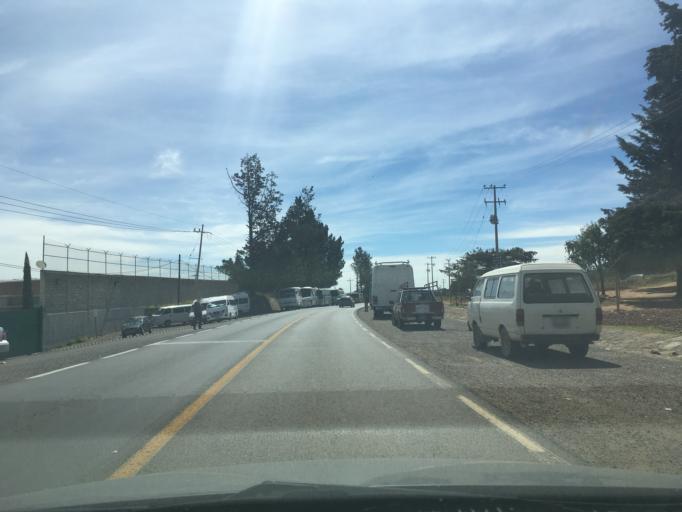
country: MX
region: Queretaro
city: Amealco
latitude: 20.1854
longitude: -100.1663
